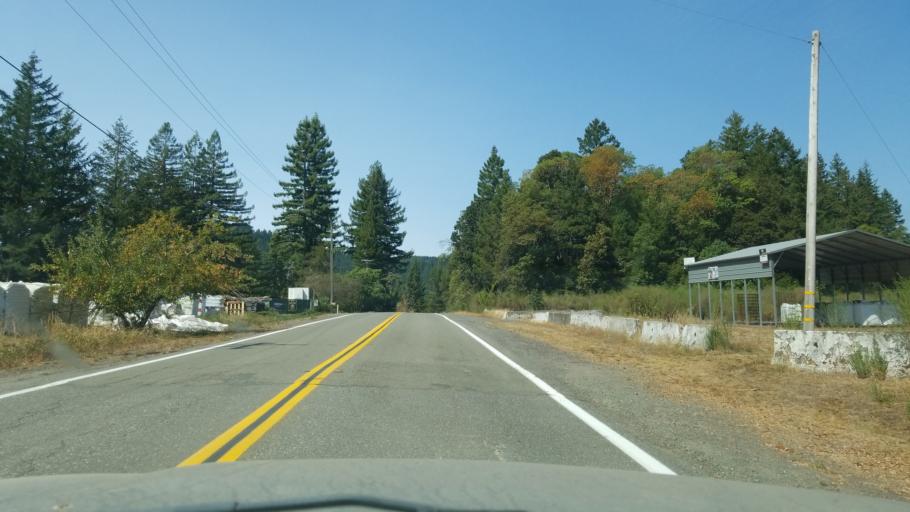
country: US
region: California
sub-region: Mendocino County
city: Laytonville
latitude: 39.8508
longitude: -123.7165
